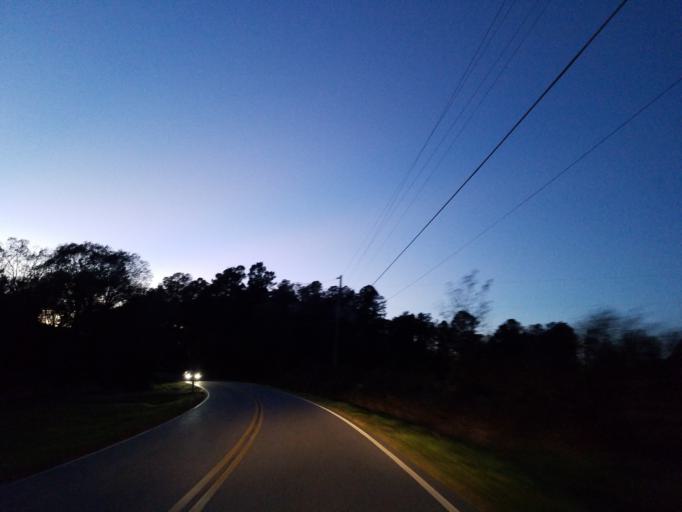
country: US
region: Georgia
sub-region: Dawson County
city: Dawsonville
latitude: 34.3301
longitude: -84.0838
